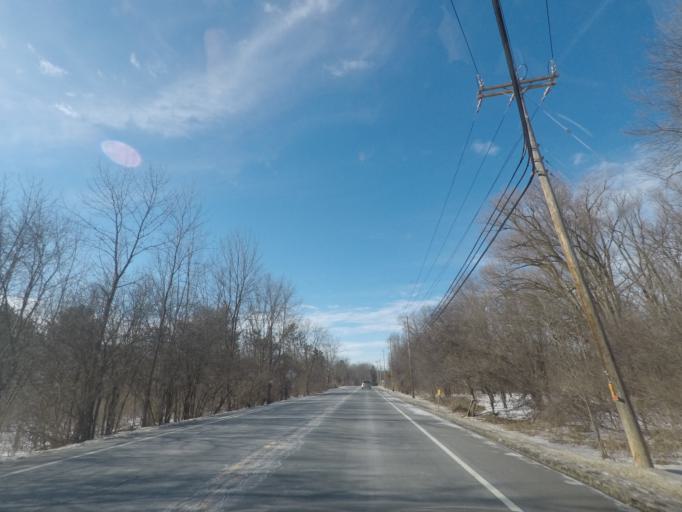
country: US
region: New York
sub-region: Albany County
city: Altamont
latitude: 42.7085
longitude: -73.9816
